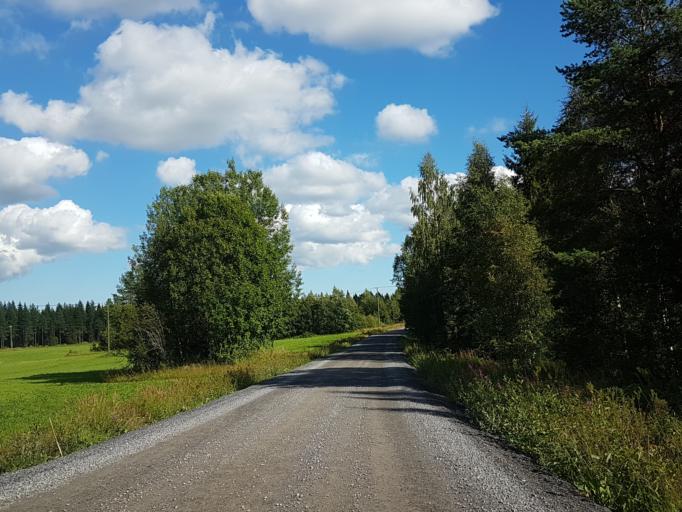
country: SE
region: Vaesterbotten
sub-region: Skelleftea Kommun
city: Burtraesk
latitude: 64.2943
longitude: 20.5164
